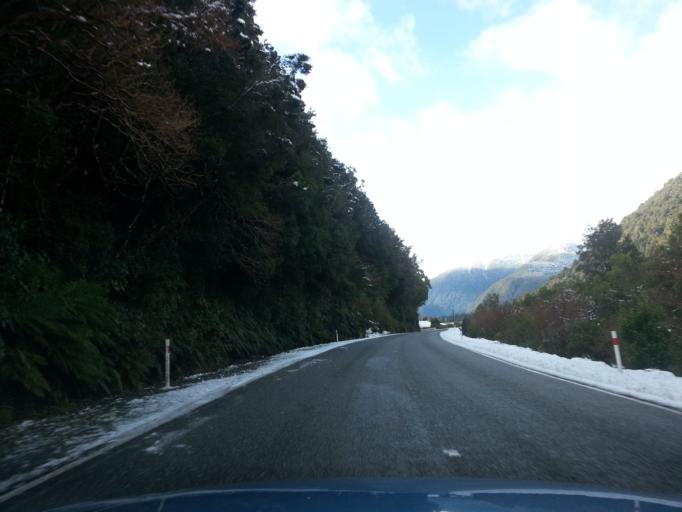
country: NZ
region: West Coast
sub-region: Grey District
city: Greymouth
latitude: -42.8074
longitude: 171.5691
